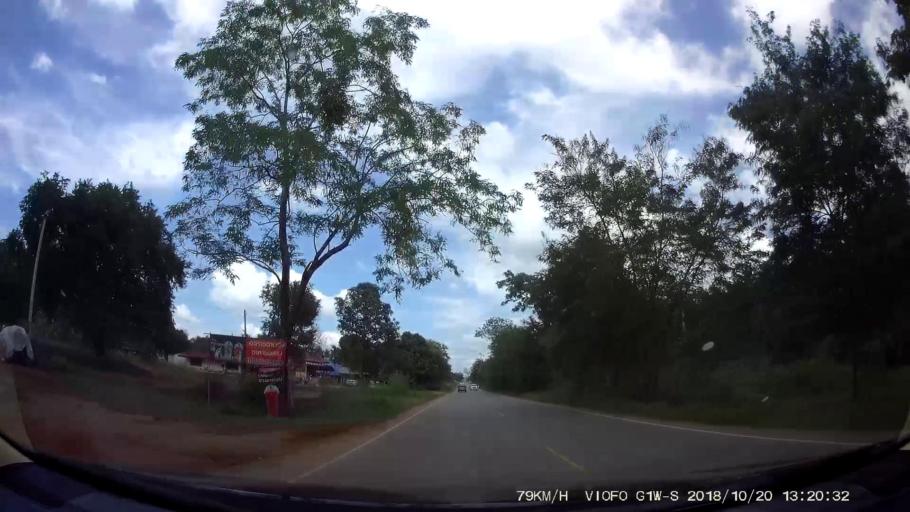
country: TH
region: Chaiyaphum
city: Khon San
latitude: 16.5493
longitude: 101.9047
